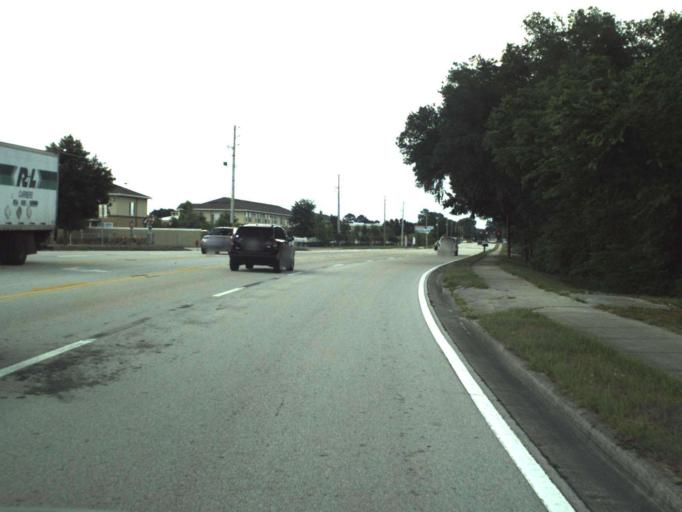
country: US
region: Florida
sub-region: Lake County
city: Leesburg
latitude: 28.8058
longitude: -81.9164
